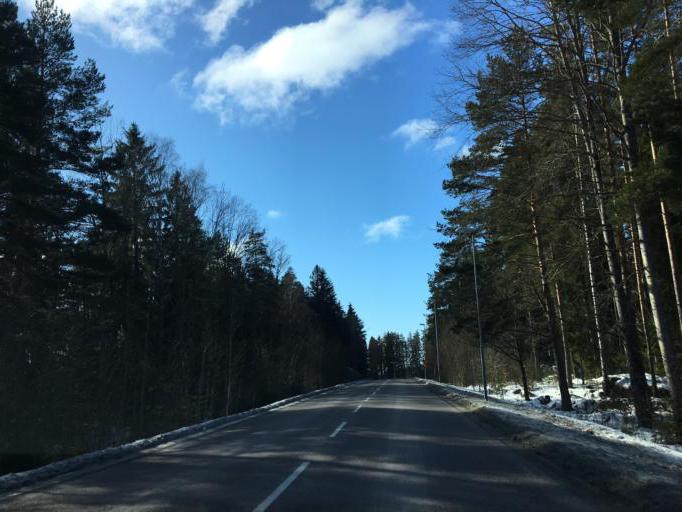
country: SE
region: Vaestmanland
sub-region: Vasteras
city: Vasteras
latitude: 59.6050
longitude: 16.4592
